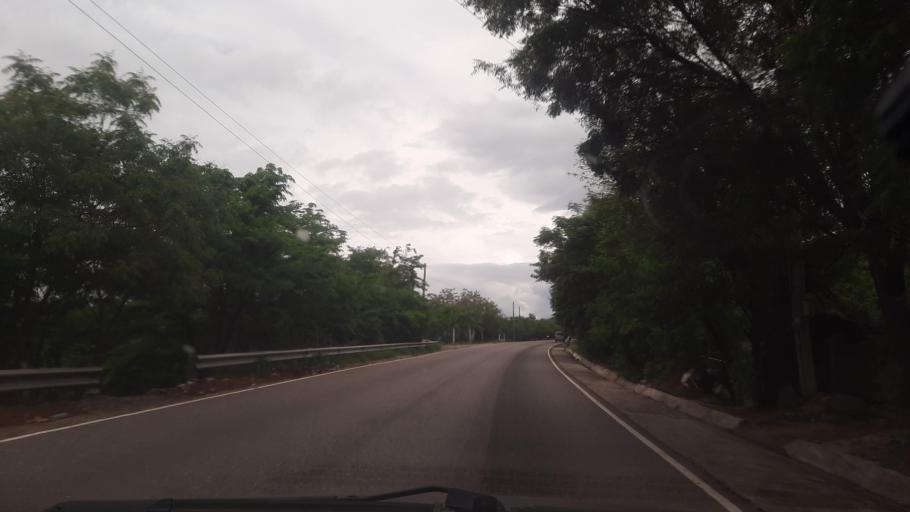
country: GT
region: Zacapa
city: San Jorge
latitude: 14.9009
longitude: -89.5224
